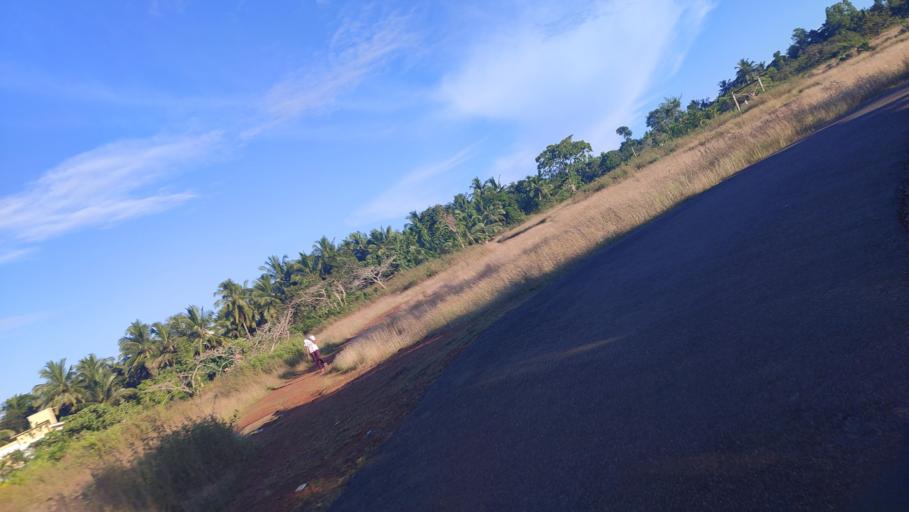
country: IN
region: Kerala
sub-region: Kasaragod District
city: Kasaragod
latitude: 12.4996
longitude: 75.0810
